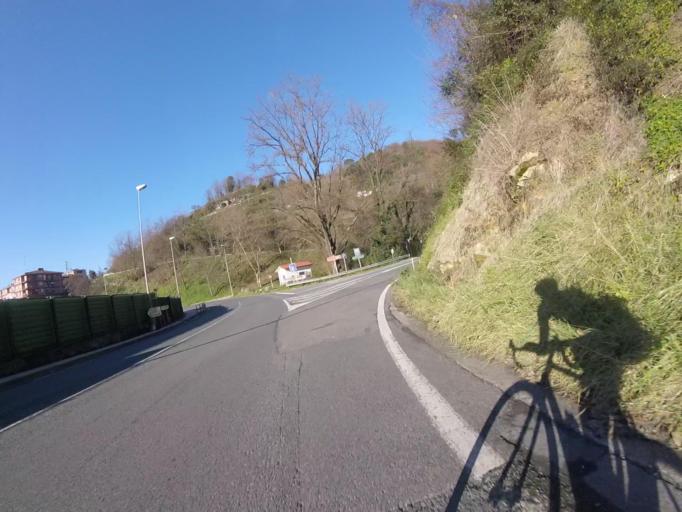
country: ES
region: Basque Country
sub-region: Provincia de Guipuzcoa
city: Lezo
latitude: 43.3244
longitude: -1.9095
